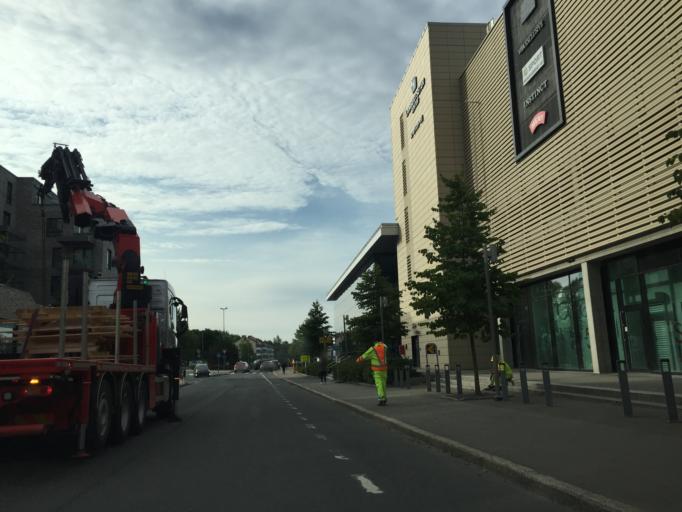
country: NO
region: Akershus
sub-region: Oppegard
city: Kolbotn
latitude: 59.8748
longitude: 10.8113
